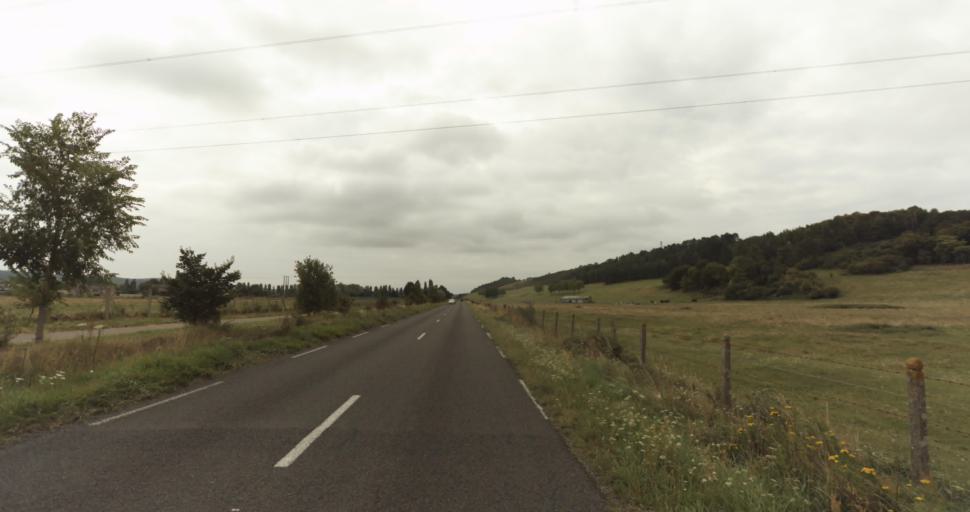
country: FR
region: Haute-Normandie
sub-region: Departement de l'Eure
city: Garennes-sur-Eure
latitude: 48.9042
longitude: 1.4465
